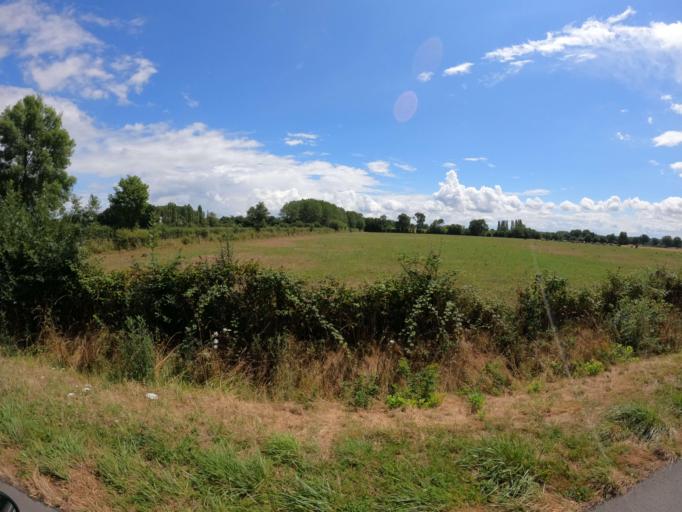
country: FR
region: Pays de la Loire
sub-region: Departement de Maine-et-Loire
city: Champigne
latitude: 47.6453
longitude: -0.5774
